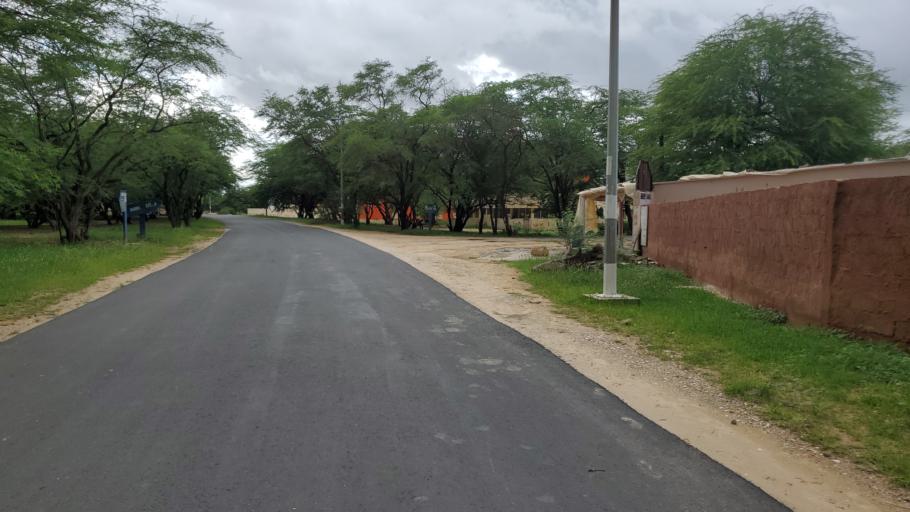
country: SN
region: Saint-Louis
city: Saint-Louis
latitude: 16.0649
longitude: -16.4195
